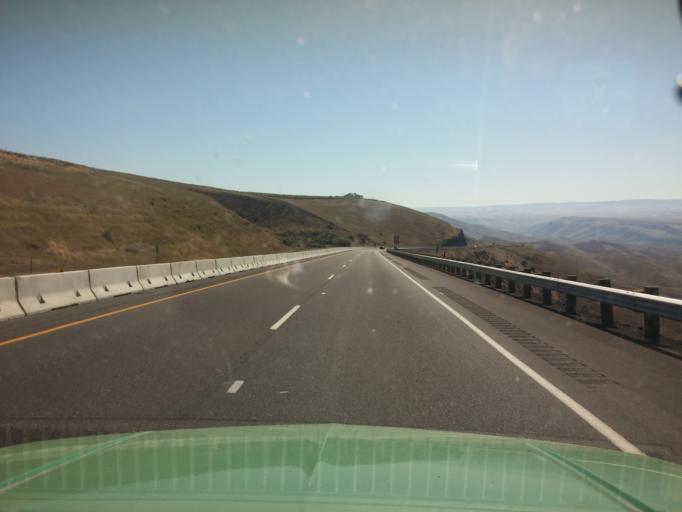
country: US
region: Idaho
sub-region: Nez Perce County
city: Lewiston
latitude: 46.4625
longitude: -117.0007
